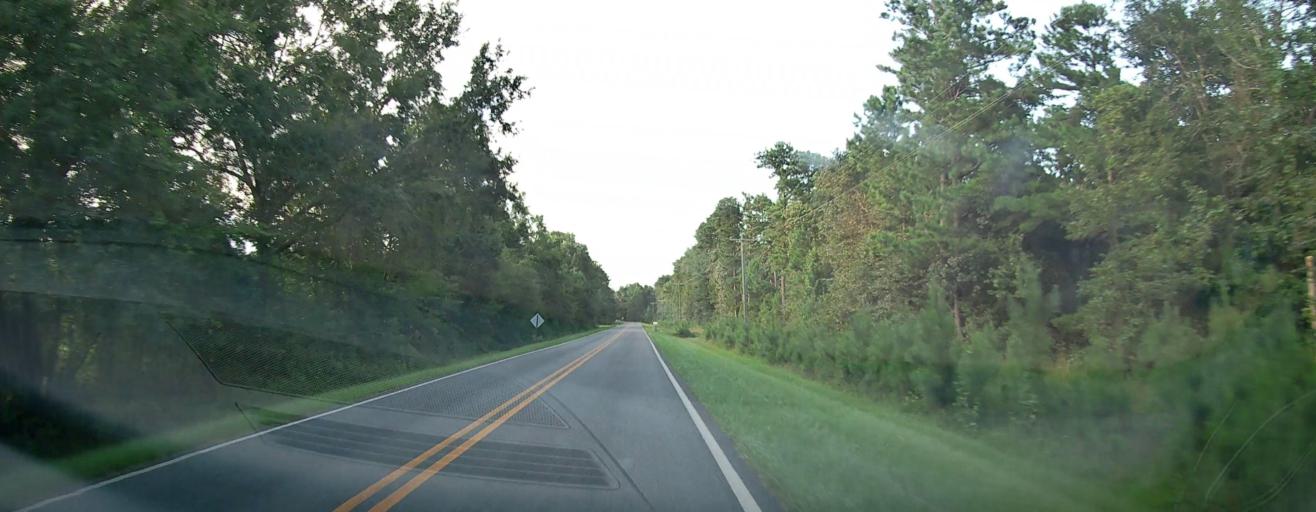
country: US
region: Georgia
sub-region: Pulaski County
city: Hawkinsville
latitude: 32.2900
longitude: -83.5531
